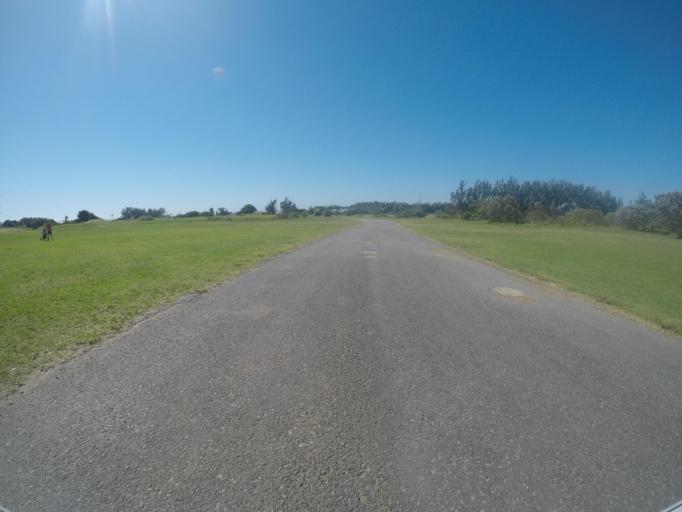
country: ZA
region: Eastern Cape
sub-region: Buffalo City Metropolitan Municipality
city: East London
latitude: -32.9502
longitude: 28.0052
